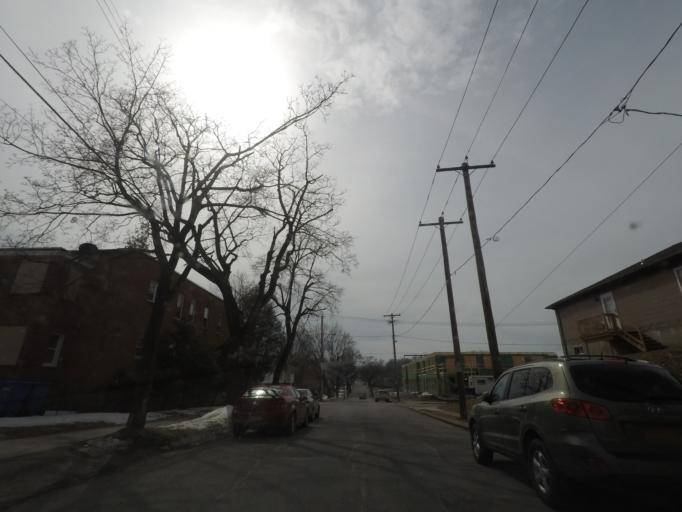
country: US
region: New York
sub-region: Albany County
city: West Albany
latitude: 42.6586
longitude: -73.7841
